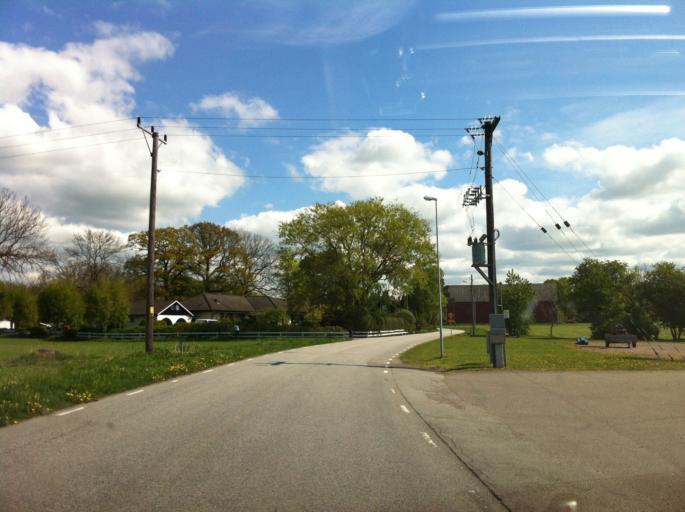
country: SE
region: Skane
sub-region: Helsingborg
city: Barslov
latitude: 56.0027
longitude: 12.8120
